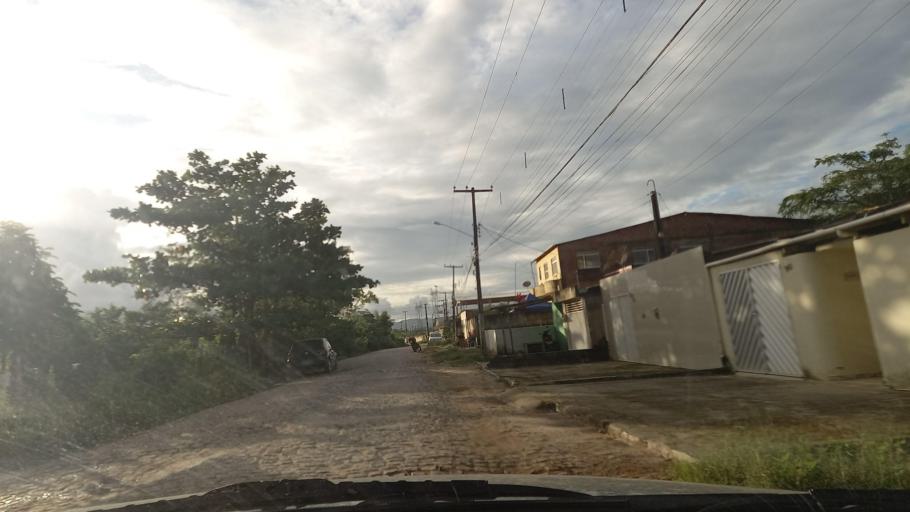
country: BR
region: Pernambuco
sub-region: Palmares
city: Palmares
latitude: -8.6796
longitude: -35.5963
